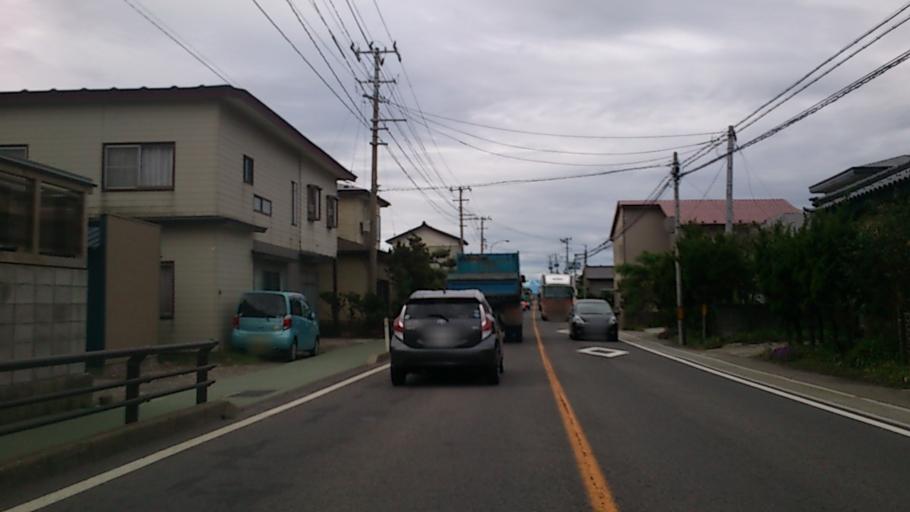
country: JP
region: Akita
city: Akita Shi
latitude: 39.6212
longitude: 140.0643
